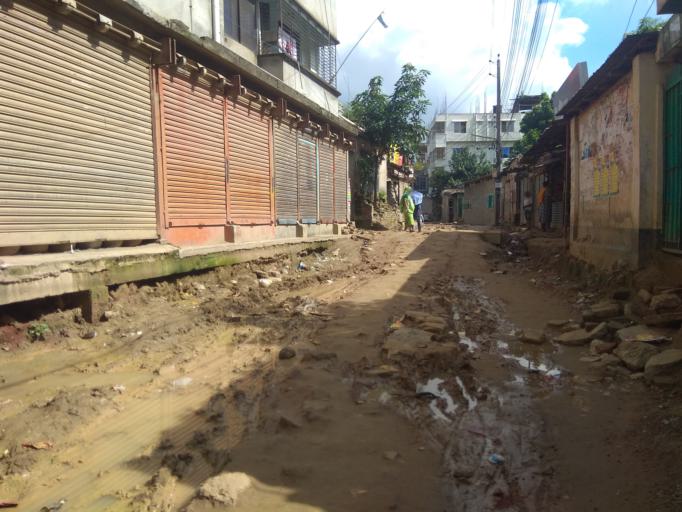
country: BD
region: Dhaka
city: Tungi
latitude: 23.8141
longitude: 90.3874
